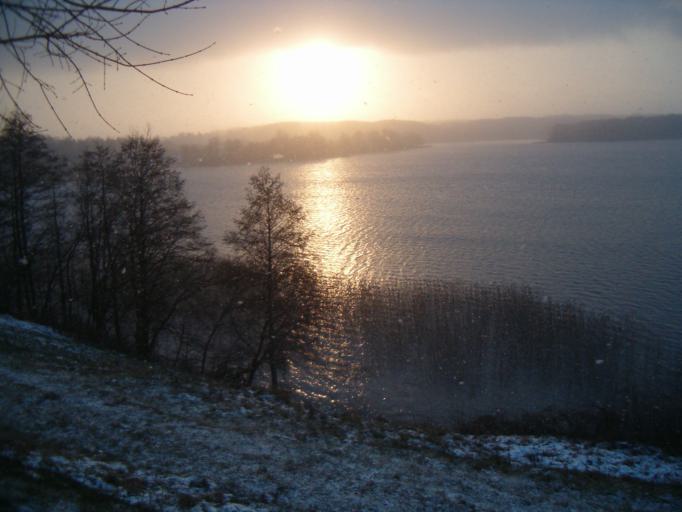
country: LT
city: Zarasai
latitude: 55.6346
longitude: 26.0688
